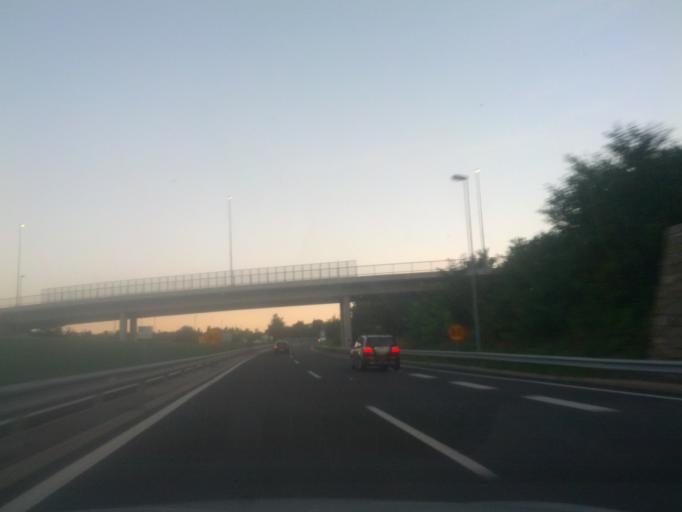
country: SI
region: Koper-Capodistria
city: Spodnje Skofije
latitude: 45.5780
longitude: 13.7962
